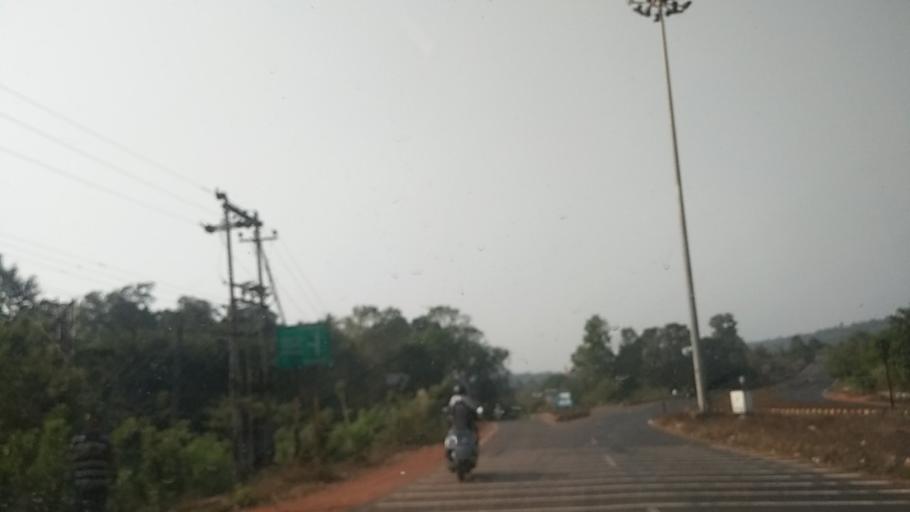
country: IN
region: Goa
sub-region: North Goa
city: Pernem
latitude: 15.7120
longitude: 73.8112
